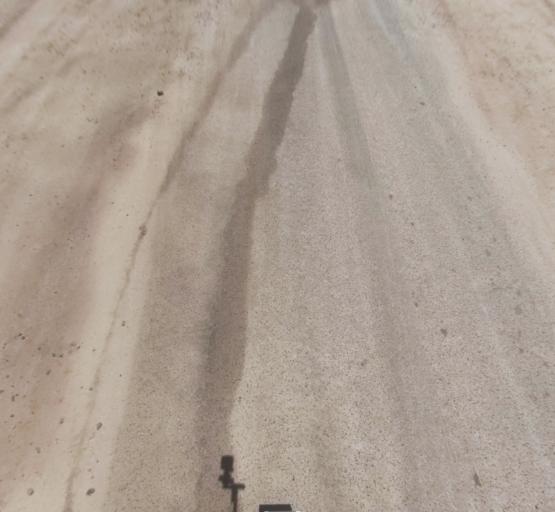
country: US
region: California
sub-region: Fresno County
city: Kerman
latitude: 36.8080
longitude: -120.1508
